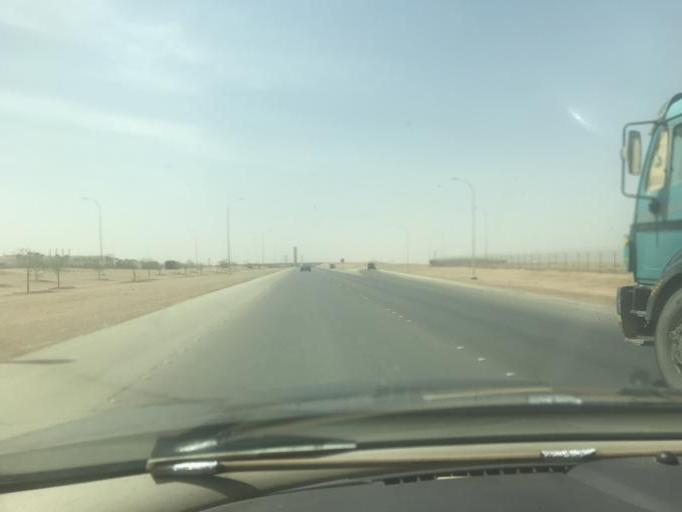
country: SA
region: Ar Riyad
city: Riyadh
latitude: 24.9750
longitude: 46.6876
